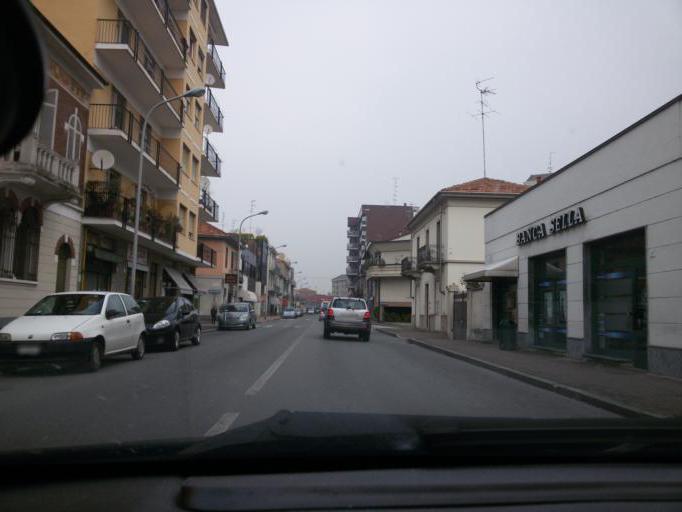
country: IT
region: Piedmont
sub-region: Provincia di Vercelli
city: Vercelli
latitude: 45.3215
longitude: 8.4146
